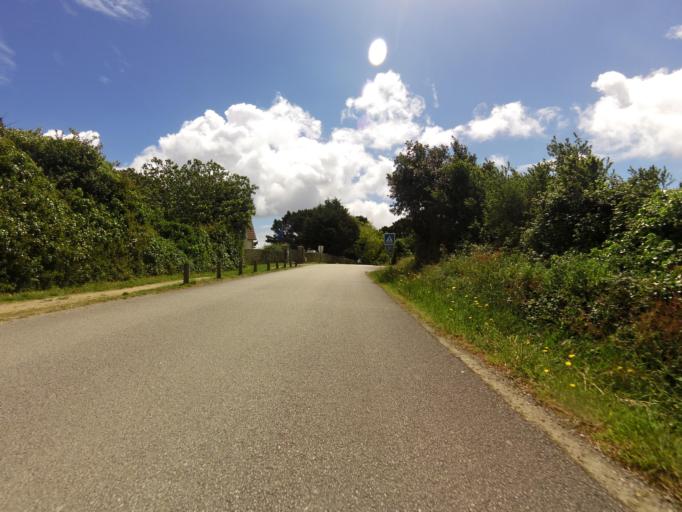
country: FR
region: Brittany
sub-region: Departement du Morbihan
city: Locmariaquer
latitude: 47.5566
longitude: -2.9296
